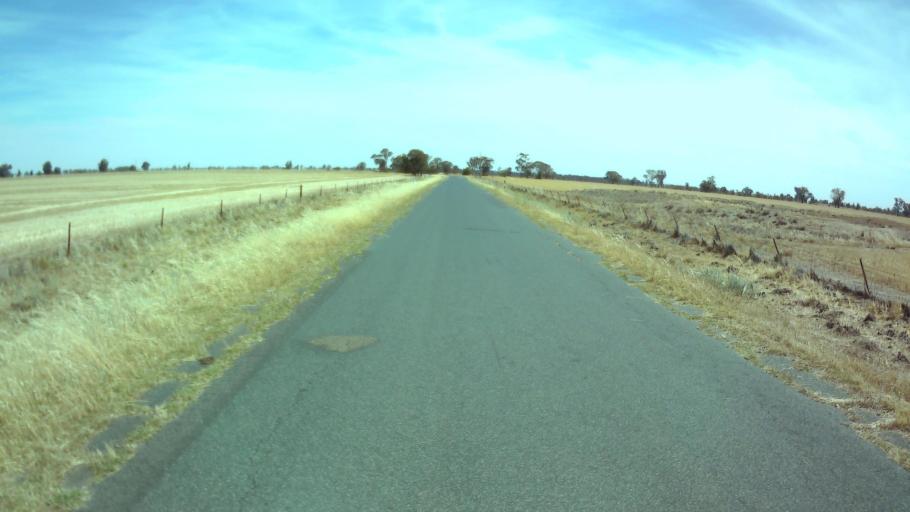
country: AU
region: New South Wales
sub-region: Weddin
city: Grenfell
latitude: -33.9328
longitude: 147.7619
